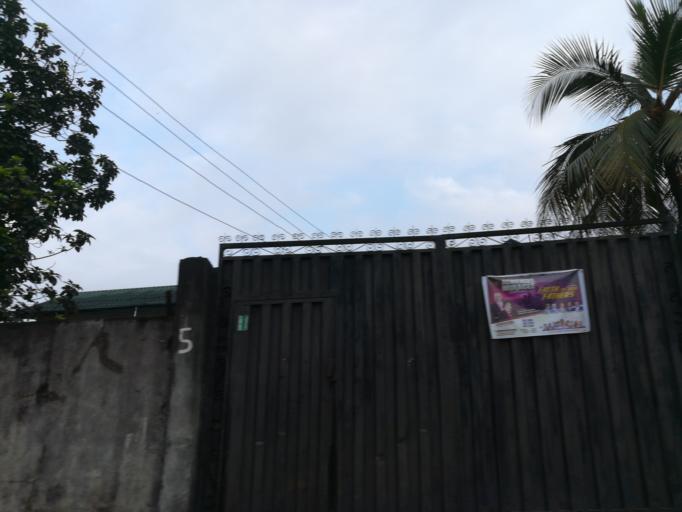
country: NG
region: Rivers
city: Port Harcourt
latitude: 4.8465
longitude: 7.0523
